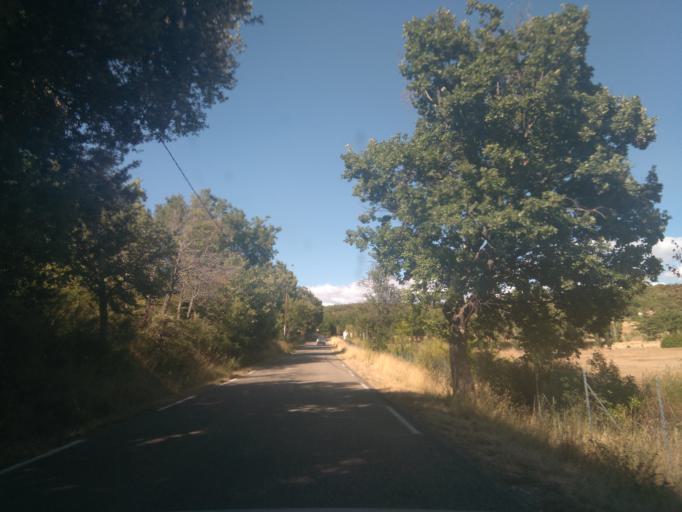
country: FR
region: Provence-Alpes-Cote d'Azur
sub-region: Departement du Var
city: Regusse
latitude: 43.7089
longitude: 6.1376
